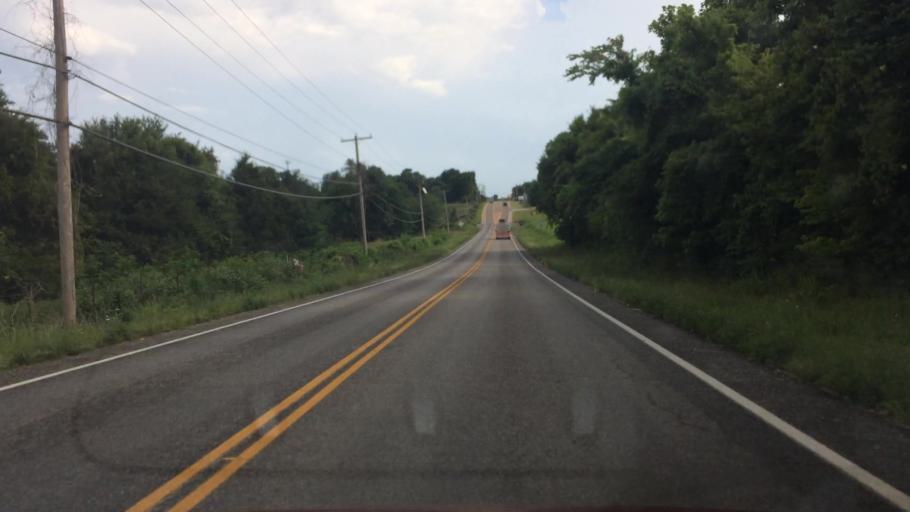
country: US
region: Missouri
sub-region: Greene County
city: Springfield
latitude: 37.2694
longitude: -93.2646
